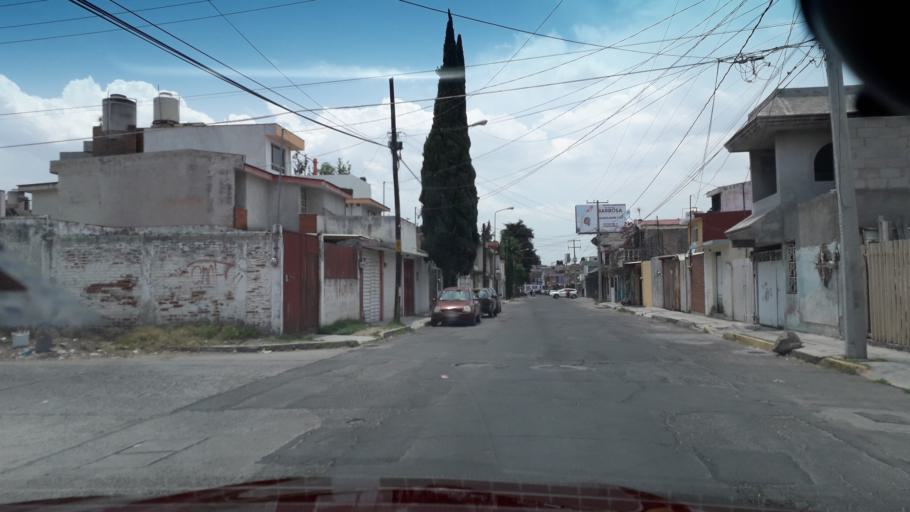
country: MX
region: Puebla
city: Tlazcalancingo
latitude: 18.9963
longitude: -98.2411
